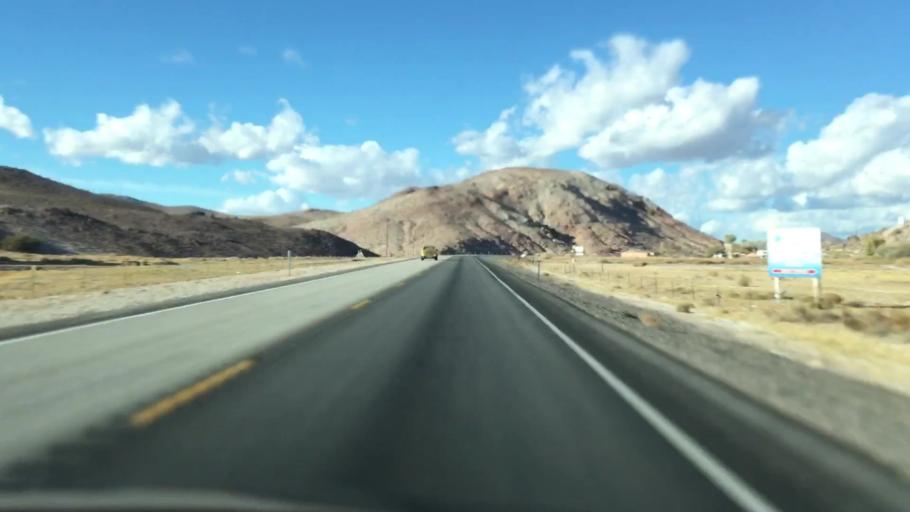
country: US
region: Nevada
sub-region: Nye County
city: Beatty
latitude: 36.9704
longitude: -116.7211
